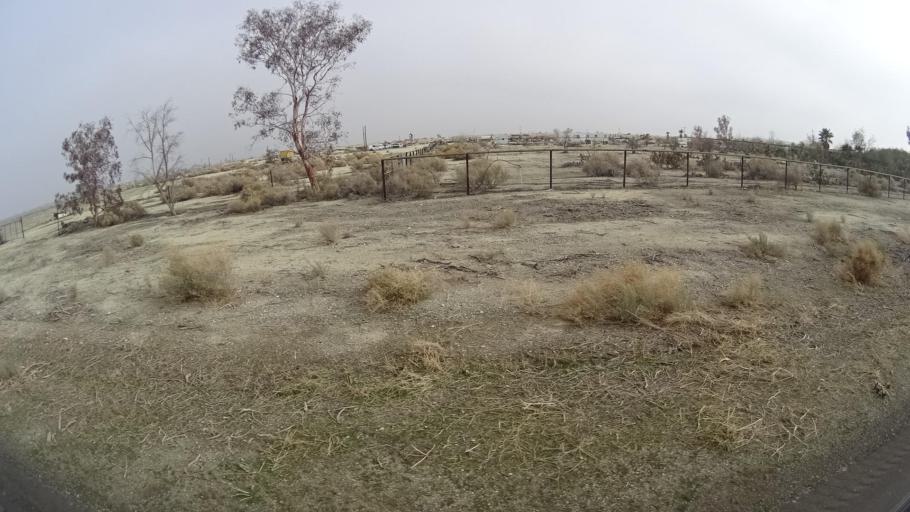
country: US
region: California
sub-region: Kern County
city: Maricopa
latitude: 35.0487
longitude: -119.3671
